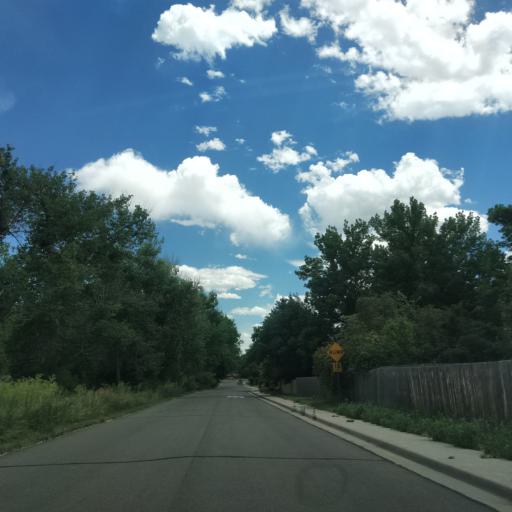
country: US
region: Colorado
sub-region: Jefferson County
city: Lakewood
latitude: 39.6885
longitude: -105.1031
